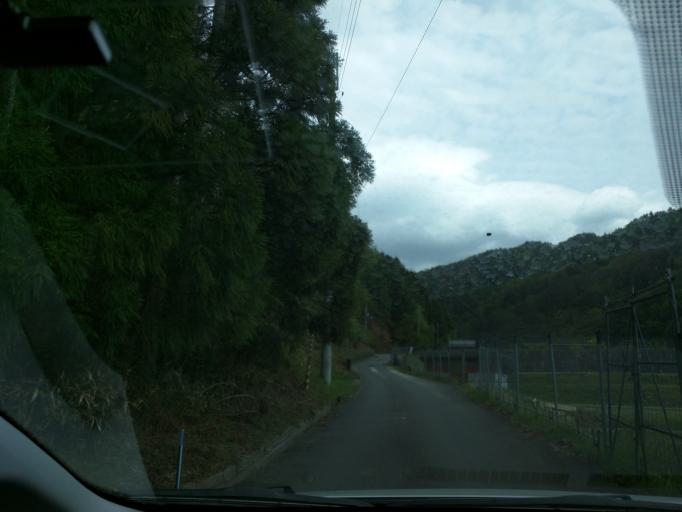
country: JP
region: Mie
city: Ueno-ebisumachi
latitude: 34.8274
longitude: 135.9940
